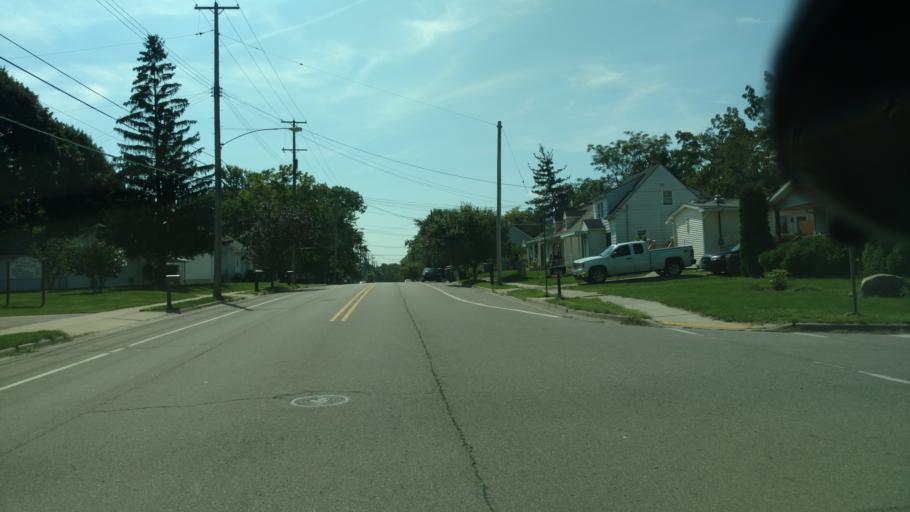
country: US
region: Michigan
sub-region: Ingham County
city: Lansing
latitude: 42.7680
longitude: -84.5558
